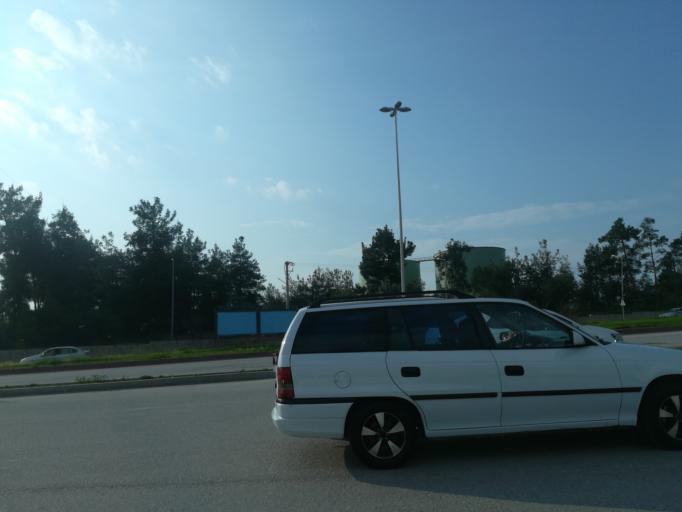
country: TR
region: Adana
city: Adana
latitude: 37.0327
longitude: 35.3466
